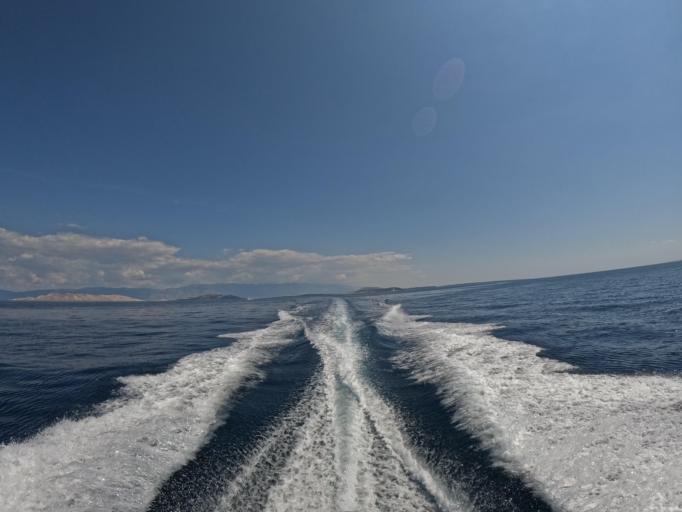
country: HR
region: Primorsko-Goranska
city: Punat
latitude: 44.8974
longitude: 14.6179
